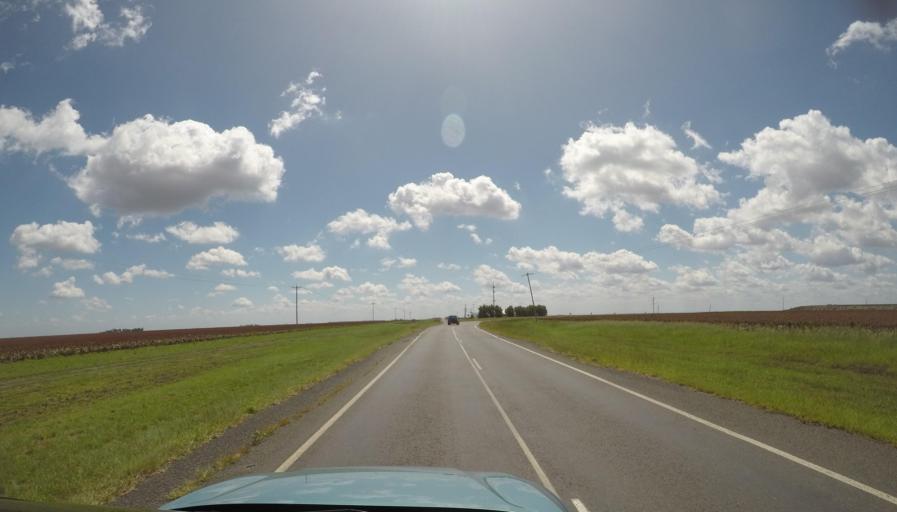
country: AU
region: Queensland
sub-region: Toowoomba
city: Oakey
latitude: -27.5174
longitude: 151.3898
